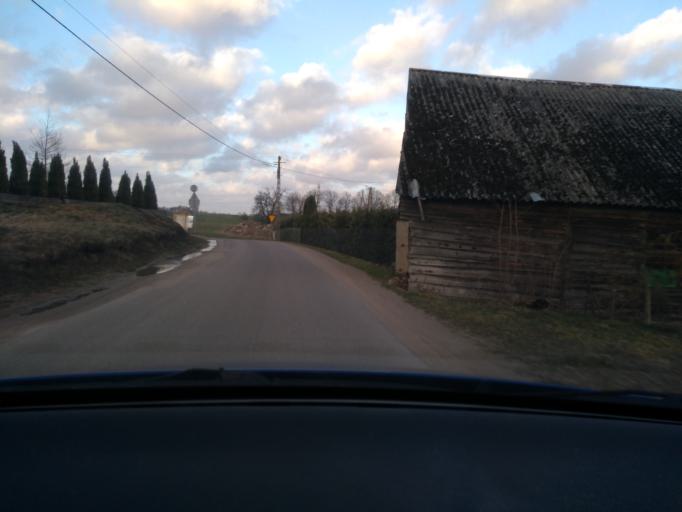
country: PL
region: Pomeranian Voivodeship
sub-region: Powiat kartuski
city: Przodkowo
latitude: 54.4186
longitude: 18.2822
